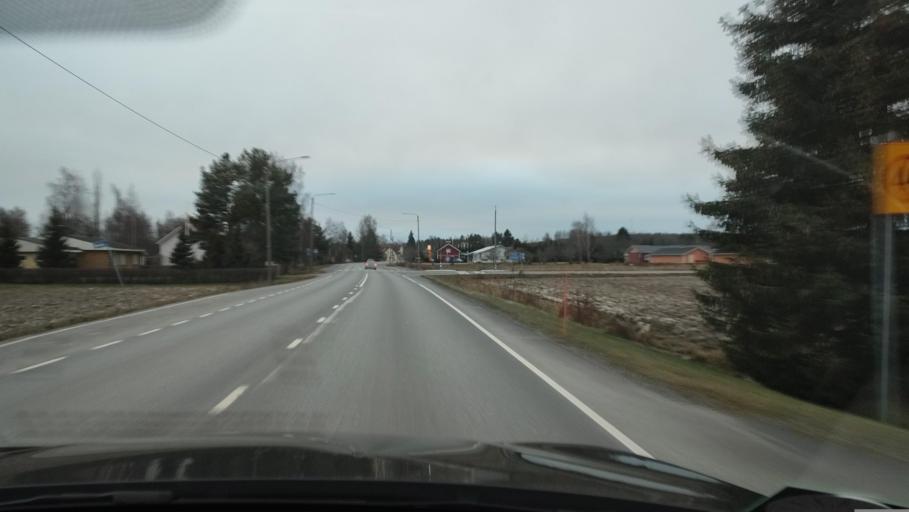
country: FI
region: Southern Ostrobothnia
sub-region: Suupohja
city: Karijoki
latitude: 62.3103
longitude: 21.7114
